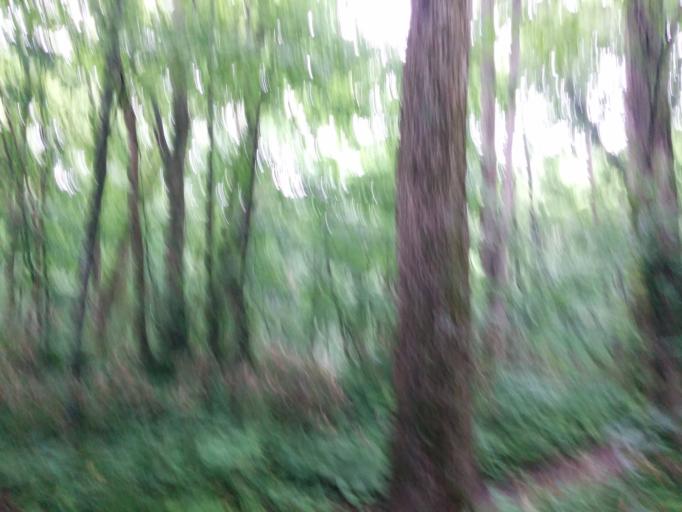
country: JP
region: Akita
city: Noshiromachi
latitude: 40.5620
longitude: 139.9813
